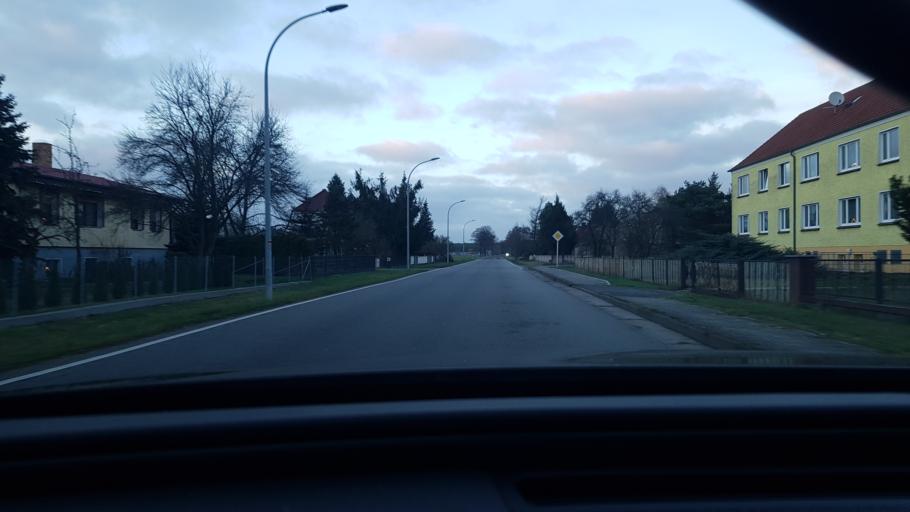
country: DE
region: Brandenburg
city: Storkow
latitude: 52.2855
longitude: 13.9074
